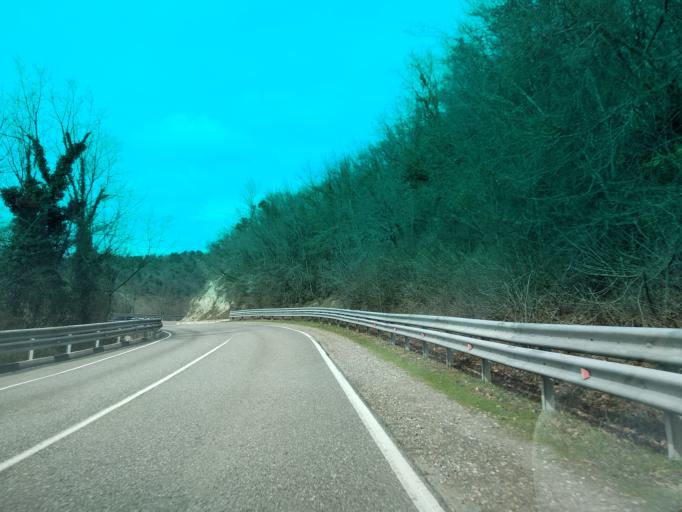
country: RU
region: Krasnodarskiy
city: Shepsi
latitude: 44.0513
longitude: 39.1316
